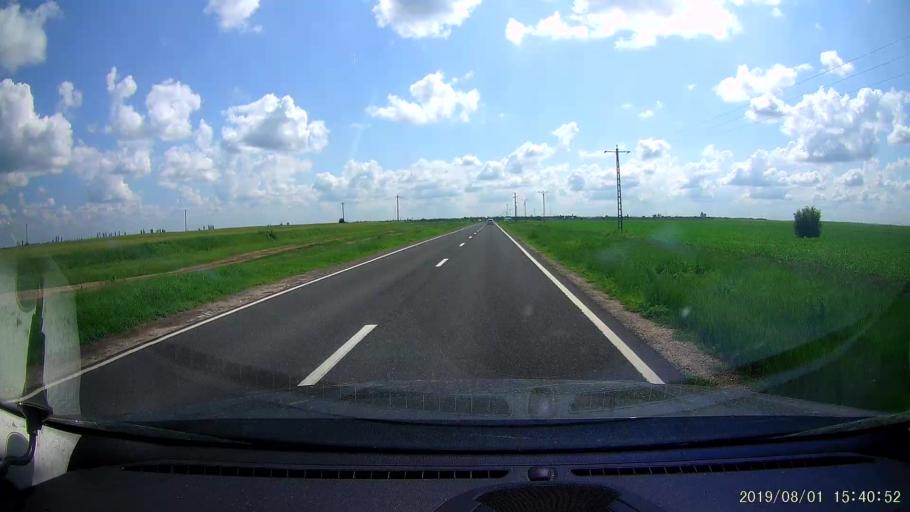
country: RO
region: Braila
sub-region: Comuna Baraganul
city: Baraganul
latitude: 44.8306
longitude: 27.5357
